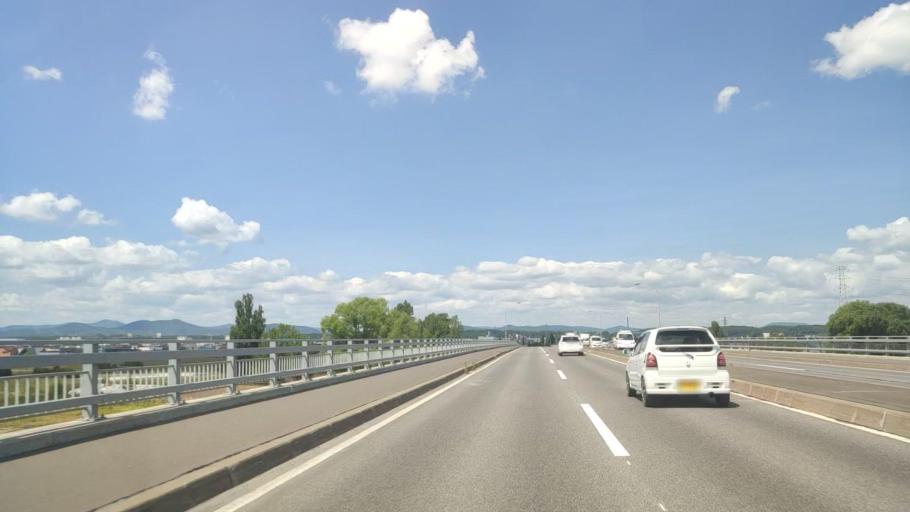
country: JP
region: Hokkaido
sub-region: Asahikawa-shi
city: Asahikawa
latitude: 43.7972
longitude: 142.3969
